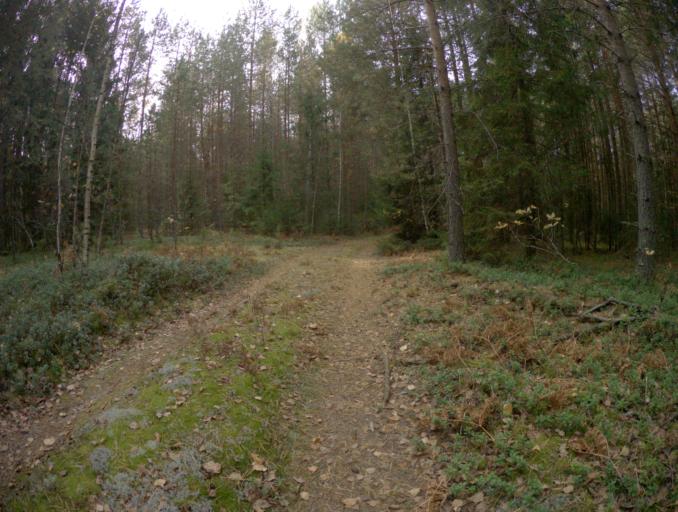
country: RU
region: Vladimir
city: Vorsha
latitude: 55.9554
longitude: 40.1276
